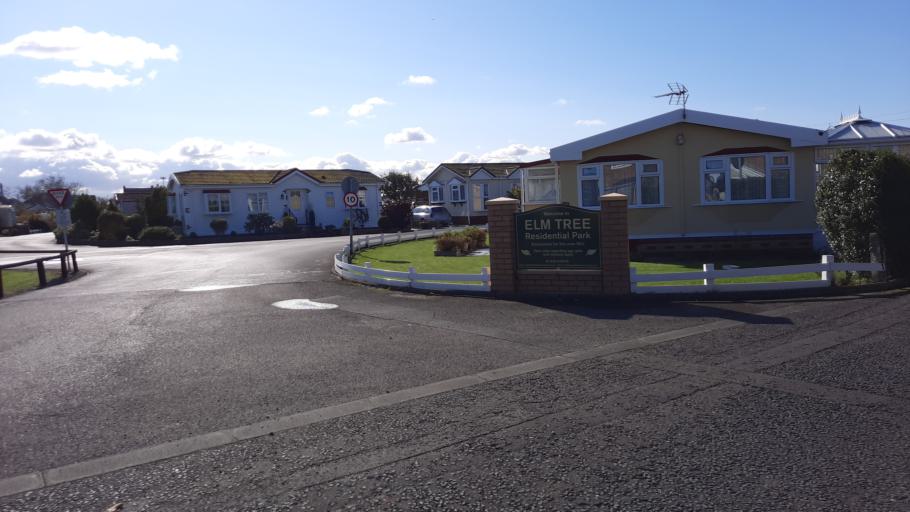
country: GB
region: England
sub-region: Hartlepool
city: Hartlepool
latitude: 54.6643
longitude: -1.1925
